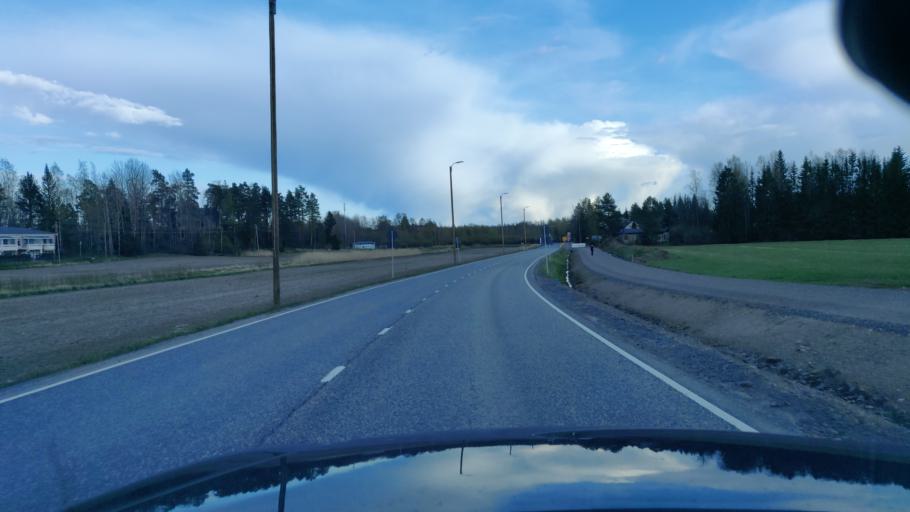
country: FI
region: Uusimaa
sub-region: Helsinki
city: Jaervenpaeae
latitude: 60.4721
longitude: 25.0690
